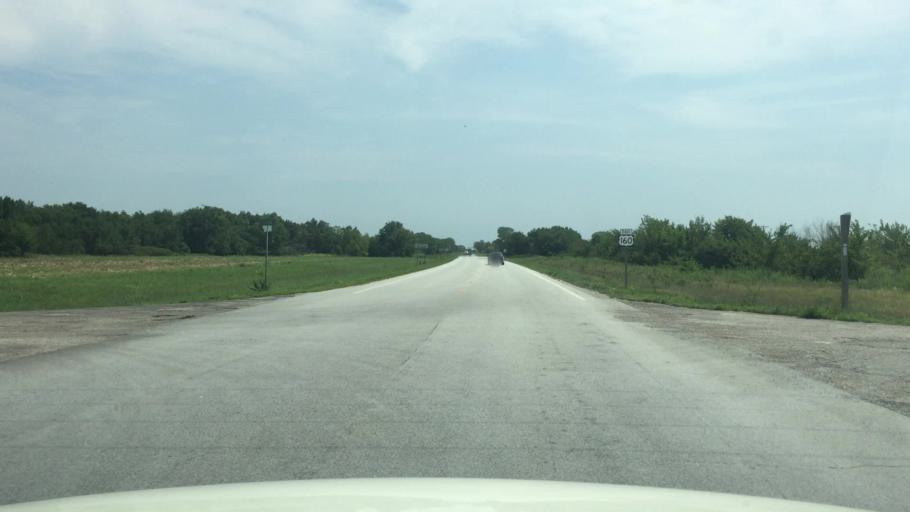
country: US
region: Kansas
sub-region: Cherokee County
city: Columbus
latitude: 37.1795
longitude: -94.9591
